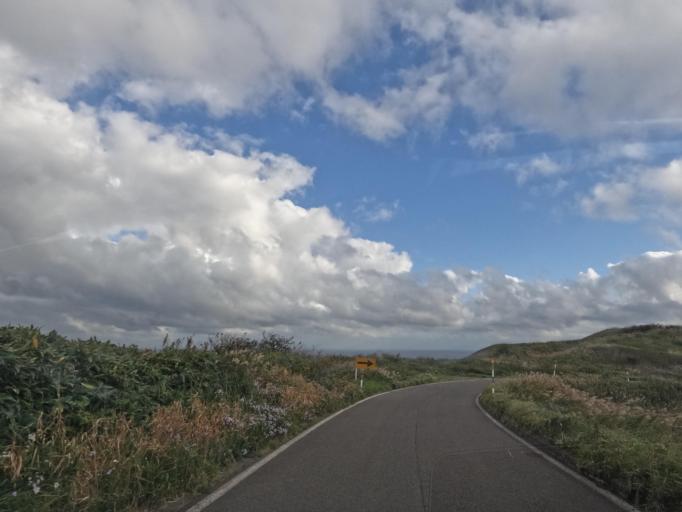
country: JP
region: Hokkaido
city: Muroran
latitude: 42.3164
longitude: 141.0066
